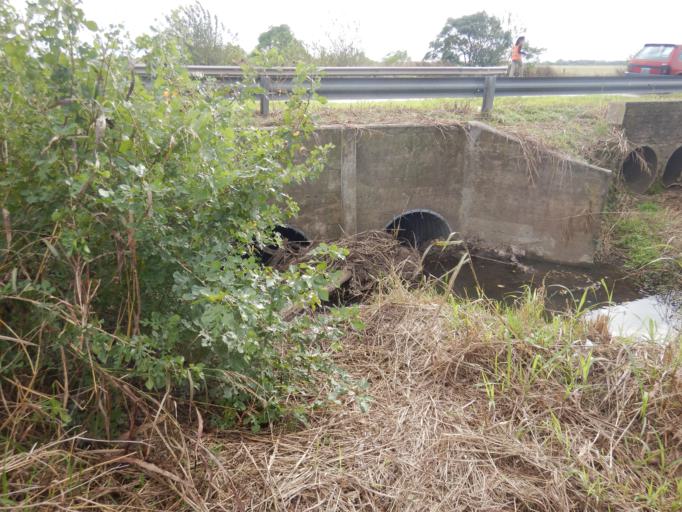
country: AR
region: Santa Fe
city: Roldan
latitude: -32.8944
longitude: -60.9716
